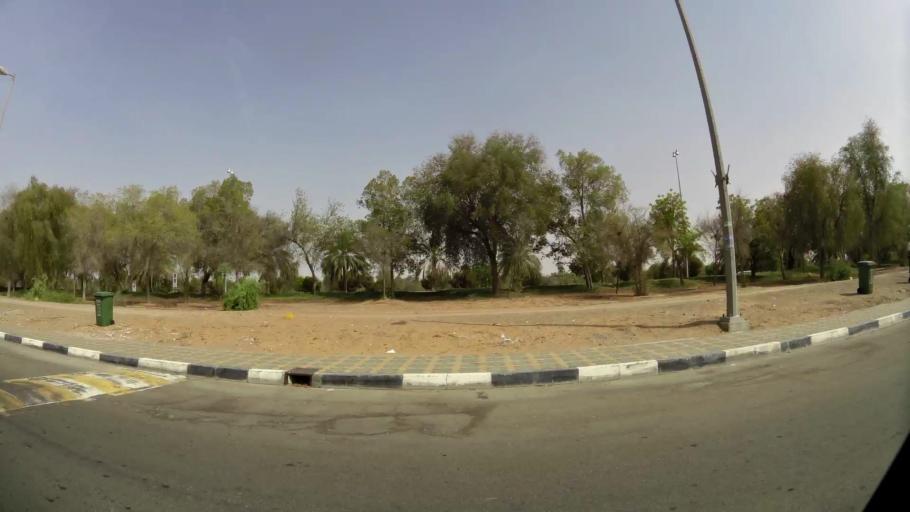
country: AE
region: Abu Dhabi
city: Al Ain
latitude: 24.1852
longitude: 55.6322
